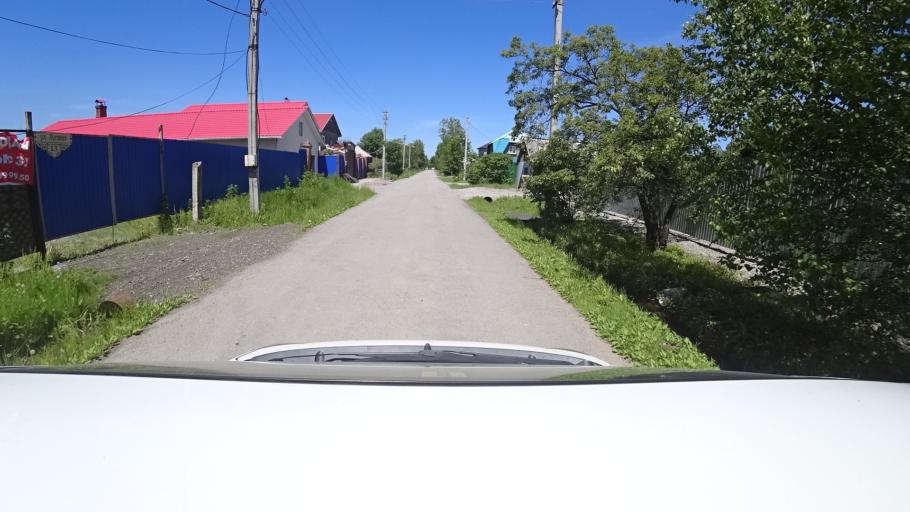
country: RU
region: Khabarovsk Krai
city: Topolevo
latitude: 48.5105
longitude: 135.1754
